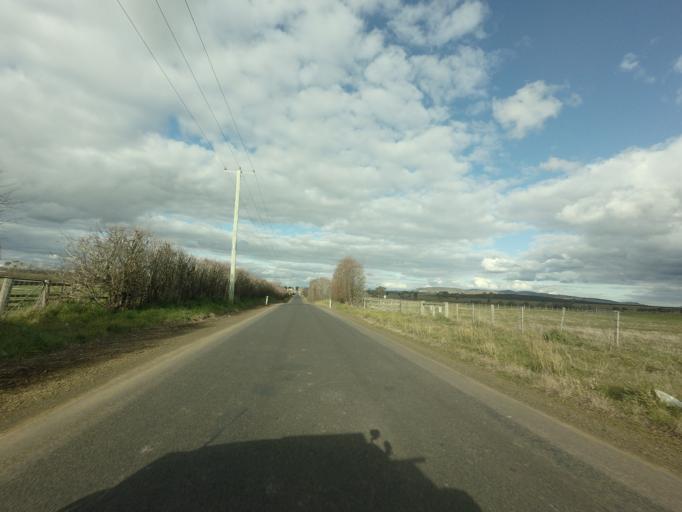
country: AU
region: Tasmania
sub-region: Northern Midlands
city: Longford
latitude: -41.8581
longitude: 147.2381
